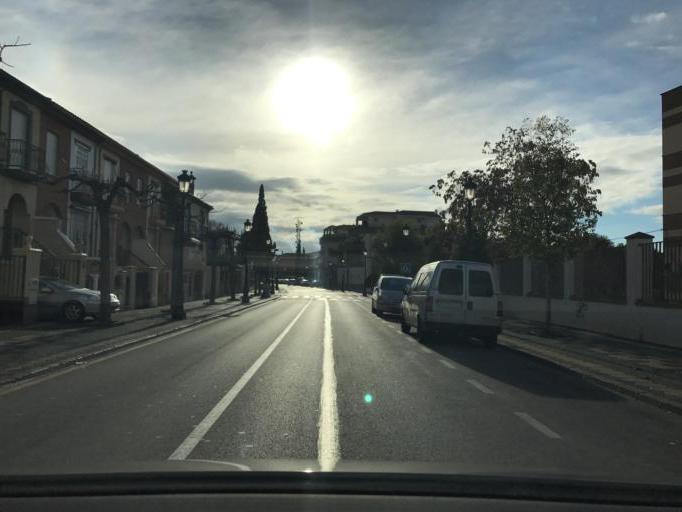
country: ES
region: Andalusia
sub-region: Provincia de Granada
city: Atarfe
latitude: 37.2185
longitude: -3.6900
